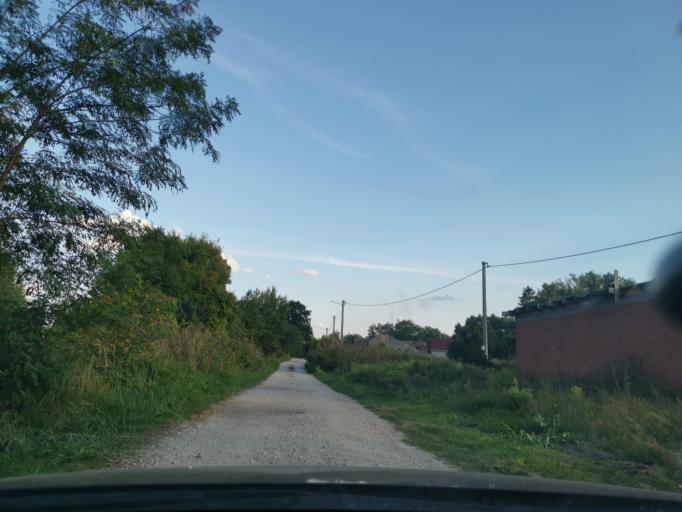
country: SK
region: Trnavsky
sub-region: Okres Senica
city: Senica
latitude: 48.6562
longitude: 17.2600
